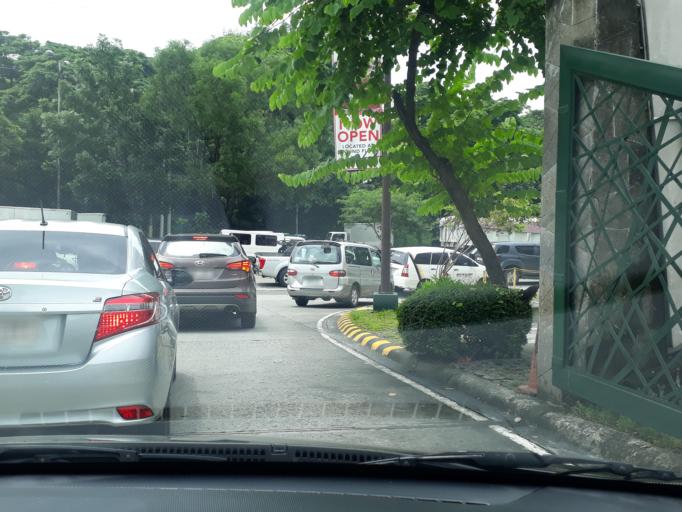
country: PH
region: Metro Manila
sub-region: Pasig
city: Pasig City
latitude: 14.5848
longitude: 121.0779
